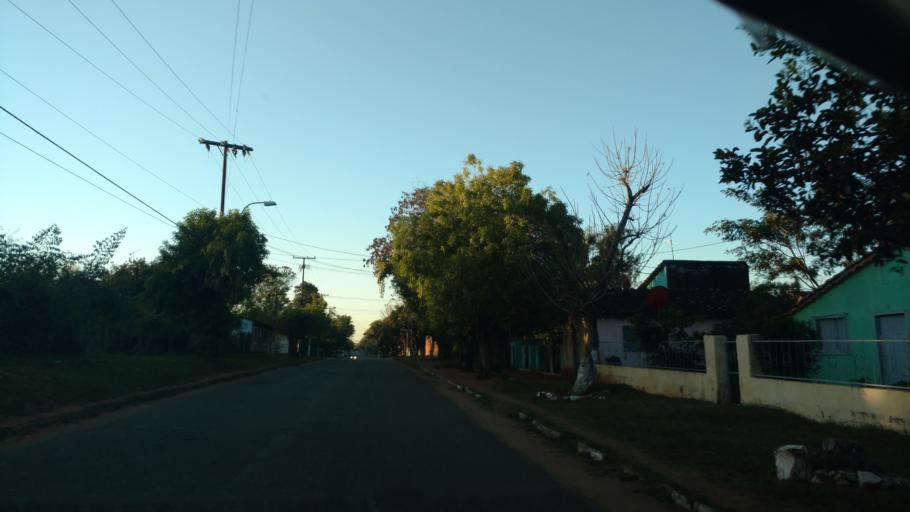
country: PY
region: Paraguari
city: Yaguaron
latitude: -25.5665
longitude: -57.2852
